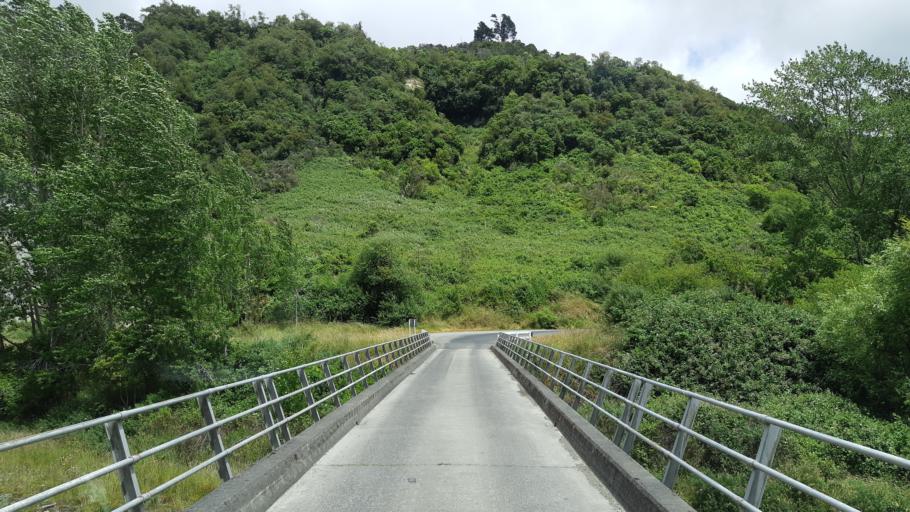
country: NZ
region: Manawatu-Wanganui
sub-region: Palmerston North City
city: Palmerston North
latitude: -39.9377
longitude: 175.9264
